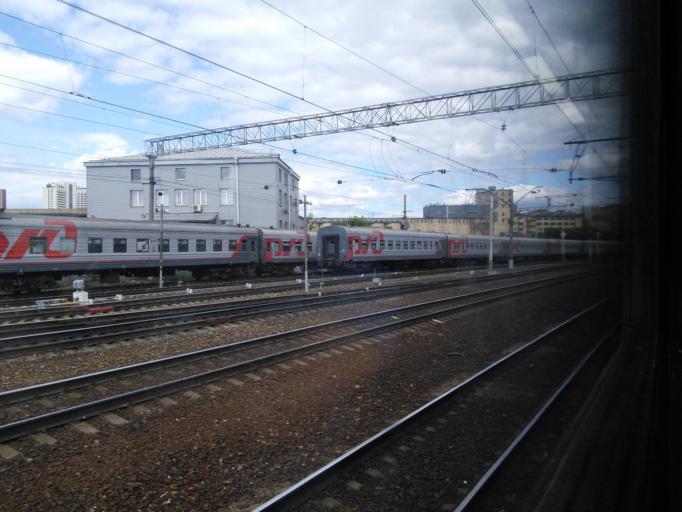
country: RU
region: Moscow
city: Sokol'niki
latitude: 55.7810
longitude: 37.6794
